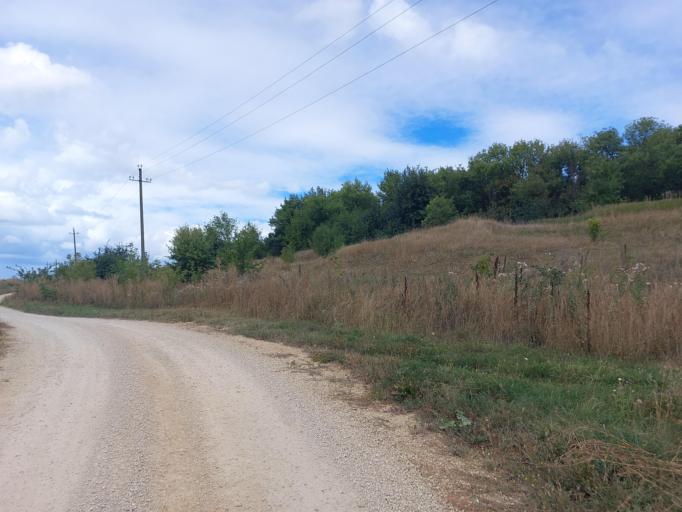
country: RU
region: Lipetsk
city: Terbuny
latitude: 52.2696
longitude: 38.2045
